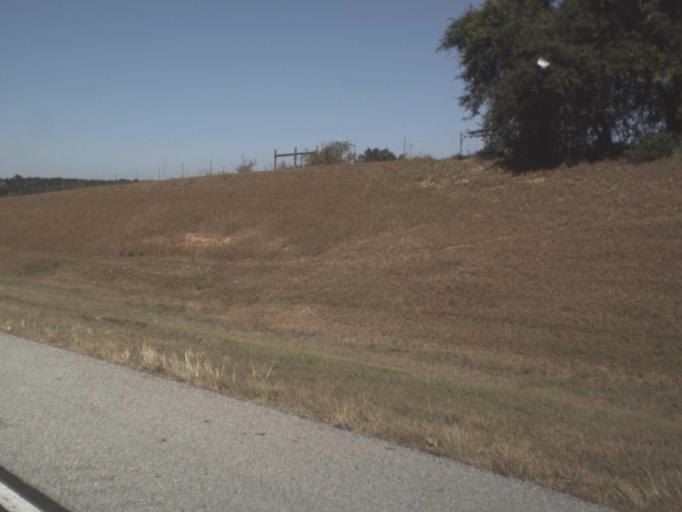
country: US
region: Florida
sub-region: Lake County
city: Minneola
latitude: 28.6175
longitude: -81.7422
